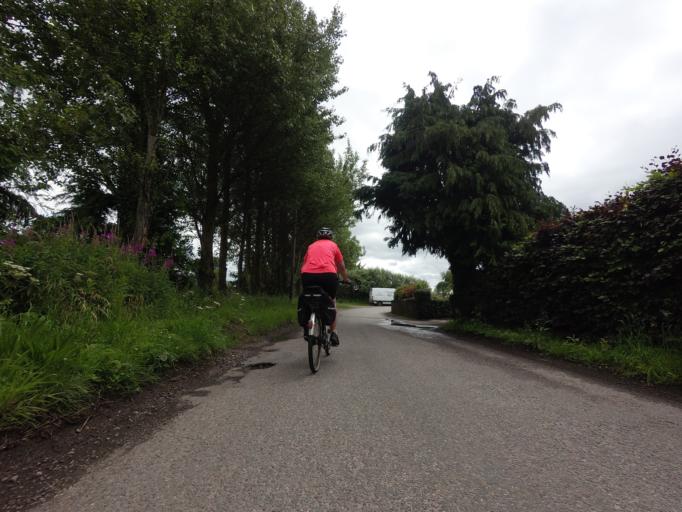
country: GB
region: Scotland
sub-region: Moray
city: Forres
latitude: 57.6150
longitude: -3.6191
